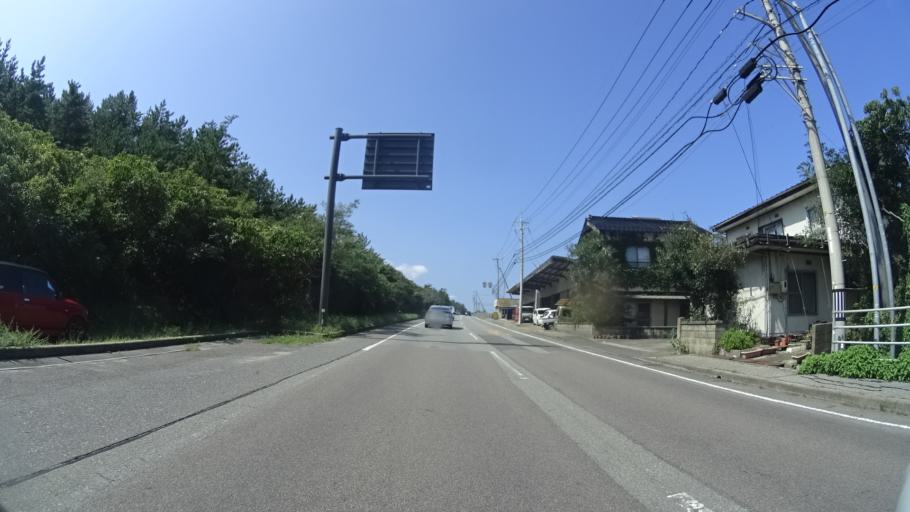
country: JP
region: Shimane
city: Masuda
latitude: 34.6883
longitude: 131.8039
